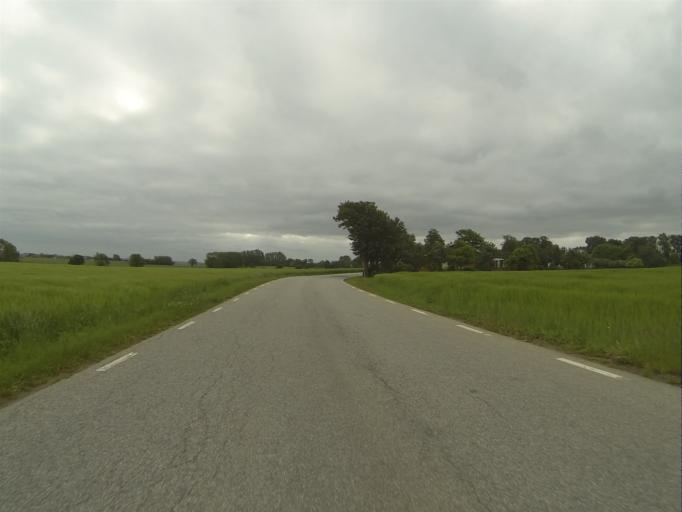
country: SE
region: Skane
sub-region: Staffanstorps Kommun
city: Staffanstorp
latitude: 55.6526
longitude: 13.2615
